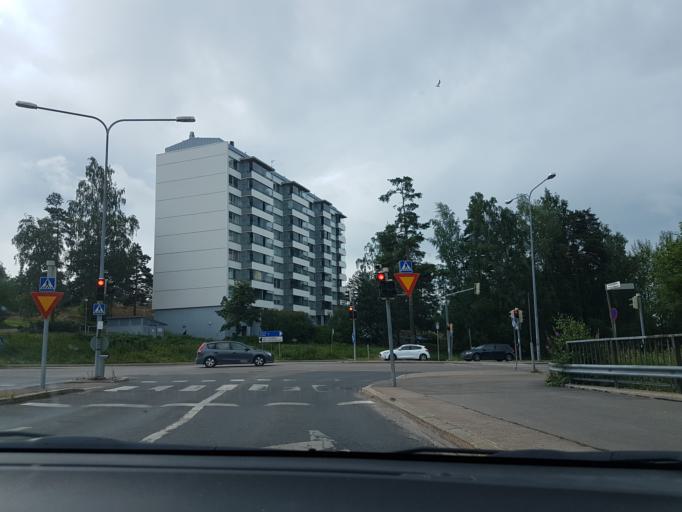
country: FI
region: Uusimaa
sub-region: Helsinki
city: Vantaa
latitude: 60.2373
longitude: 25.0883
